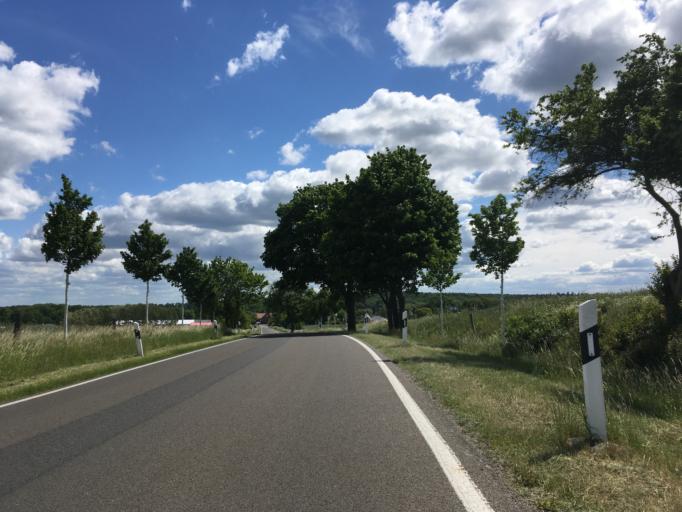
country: DE
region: Brandenburg
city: Protzel
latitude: 52.6435
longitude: 13.9882
